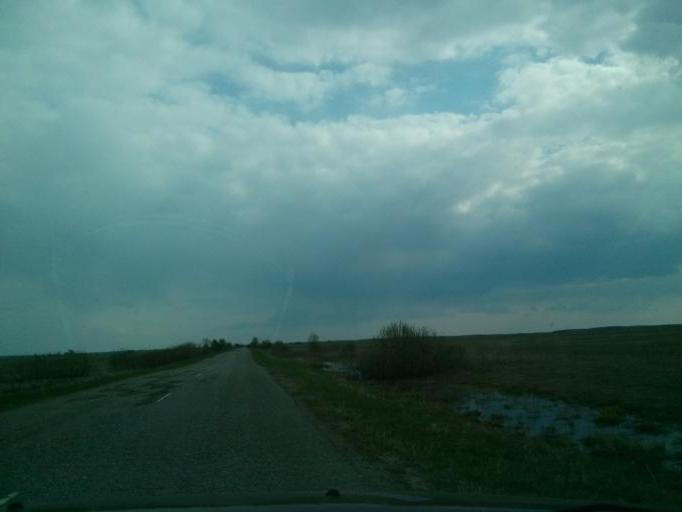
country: RU
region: Vladimir
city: Melenki
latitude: 55.3112
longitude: 41.7829
